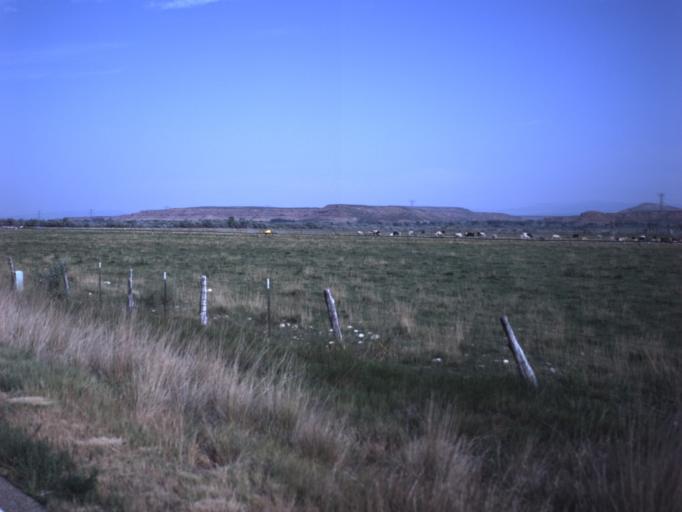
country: US
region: Utah
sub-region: Duchesne County
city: Roosevelt
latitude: 40.2585
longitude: -110.0968
